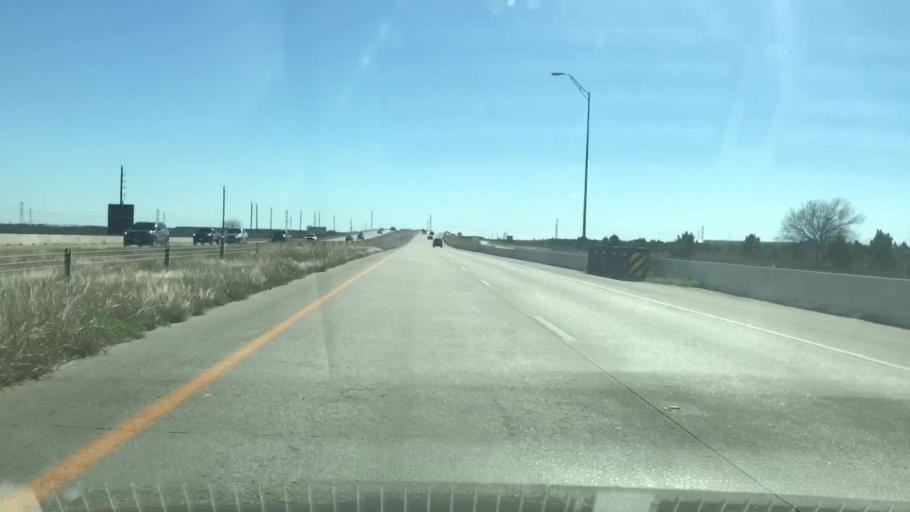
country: US
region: Texas
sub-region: Harris County
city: Cypress
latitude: 29.9272
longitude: -95.7628
